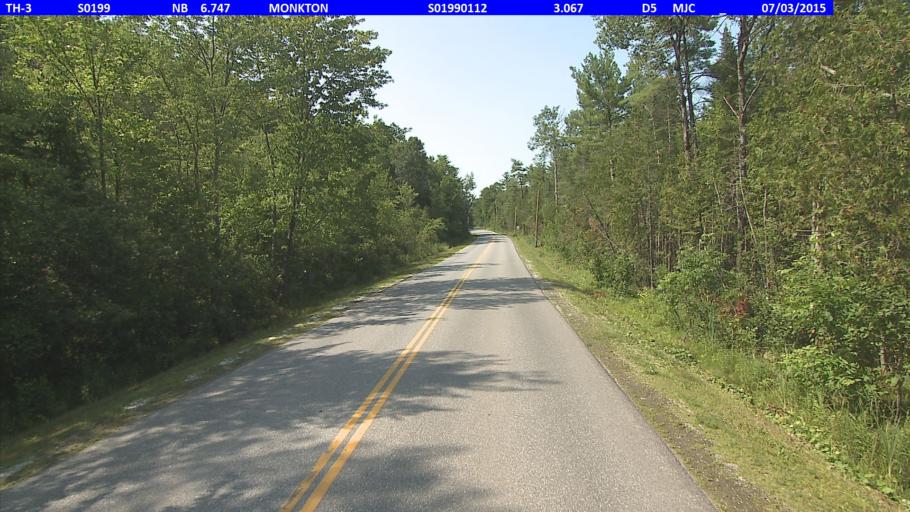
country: US
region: Vermont
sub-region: Addison County
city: Bristol
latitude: 44.2242
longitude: -73.1165
